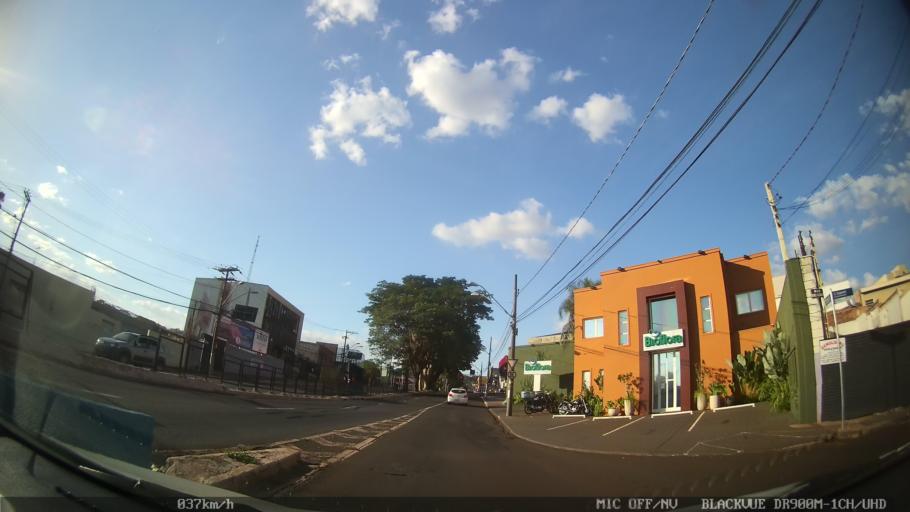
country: BR
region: Sao Paulo
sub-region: Ribeirao Preto
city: Ribeirao Preto
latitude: -21.1796
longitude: -47.7998
